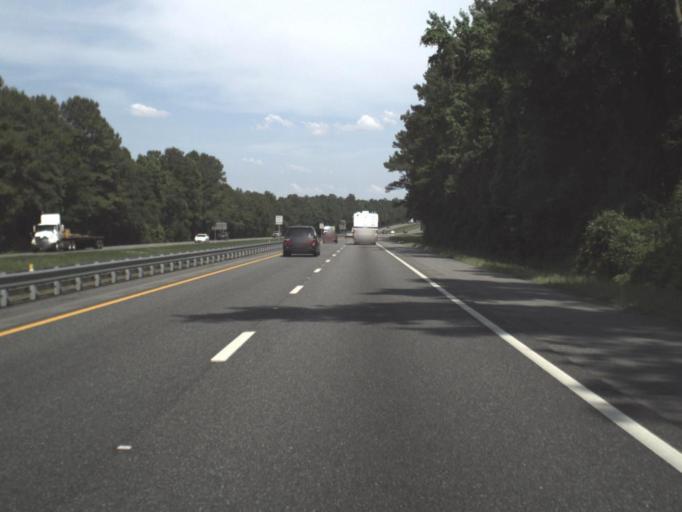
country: US
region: Florida
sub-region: Suwannee County
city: Wellborn
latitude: 30.2640
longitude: -82.7422
